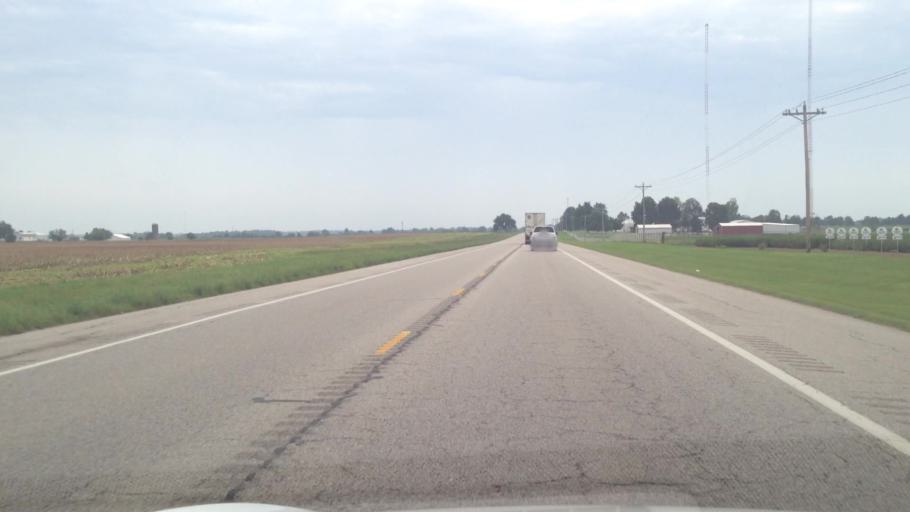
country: US
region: Missouri
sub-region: Jasper County
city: Carl Junction
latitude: 37.2276
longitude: -94.7049
